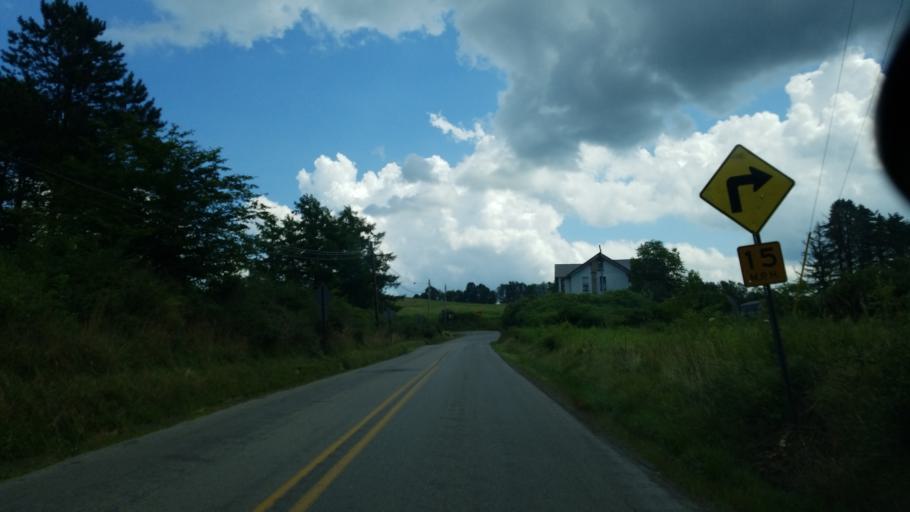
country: US
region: Pennsylvania
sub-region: Jefferson County
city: Brookville
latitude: 41.2394
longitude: -79.0115
